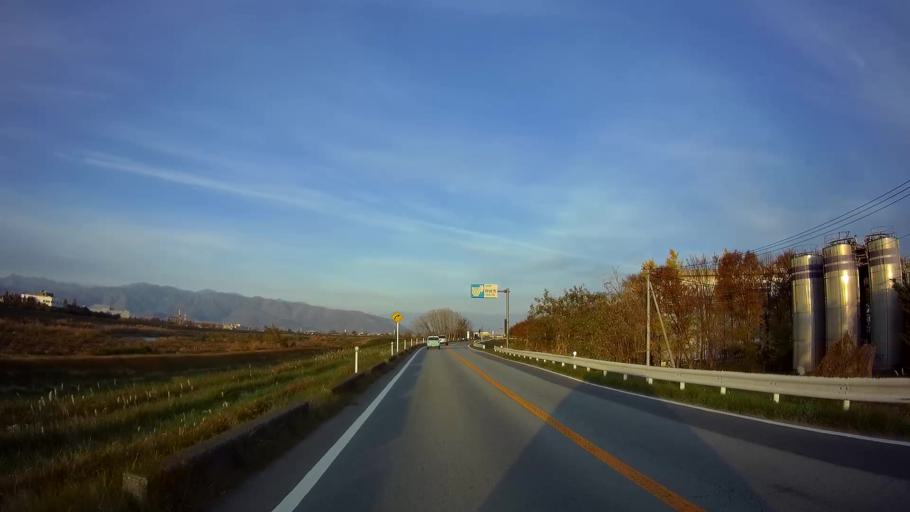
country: JP
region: Yamanashi
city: Kofu-shi
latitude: 35.5915
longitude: 138.5612
